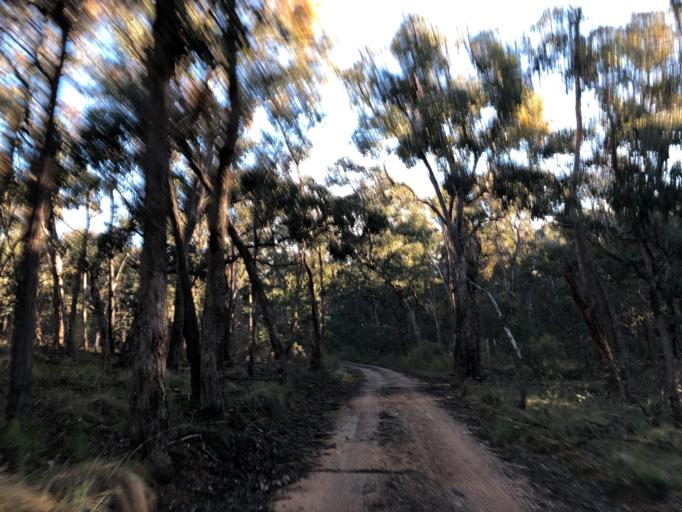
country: AU
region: Victoria
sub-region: Mount Alexander
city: Castlemaine
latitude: -37.2311
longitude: 144.2749
